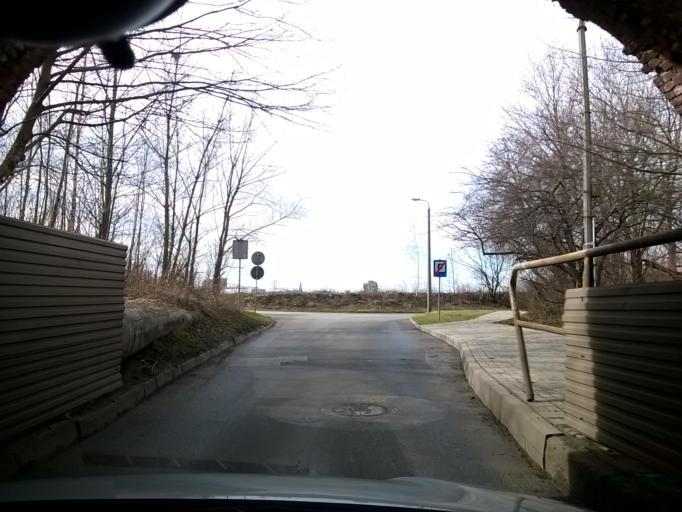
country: PL
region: Silesian Voivodeship
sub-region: Chorzow
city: Chorzow
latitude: 50.3142
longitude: 18.9608
